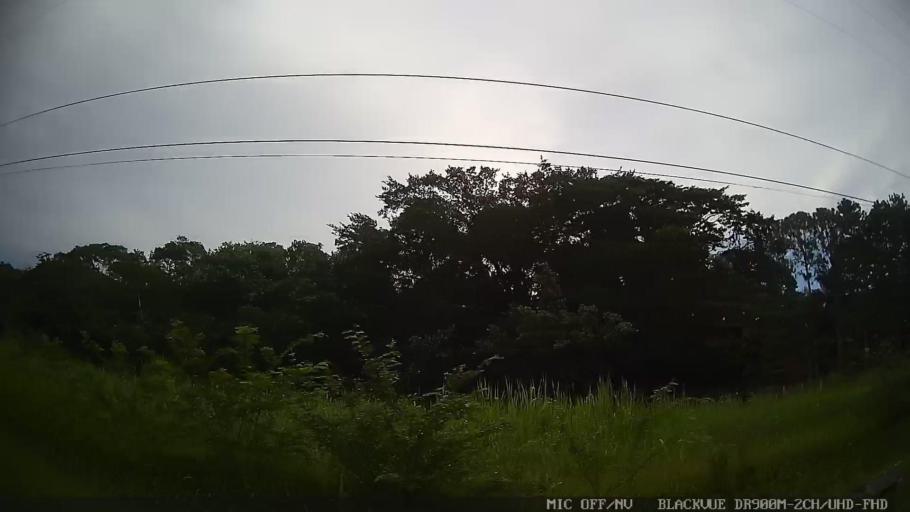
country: BR
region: Sao Paulo
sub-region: Iguape
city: Iguape
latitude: -24.6888
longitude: -47.5186
